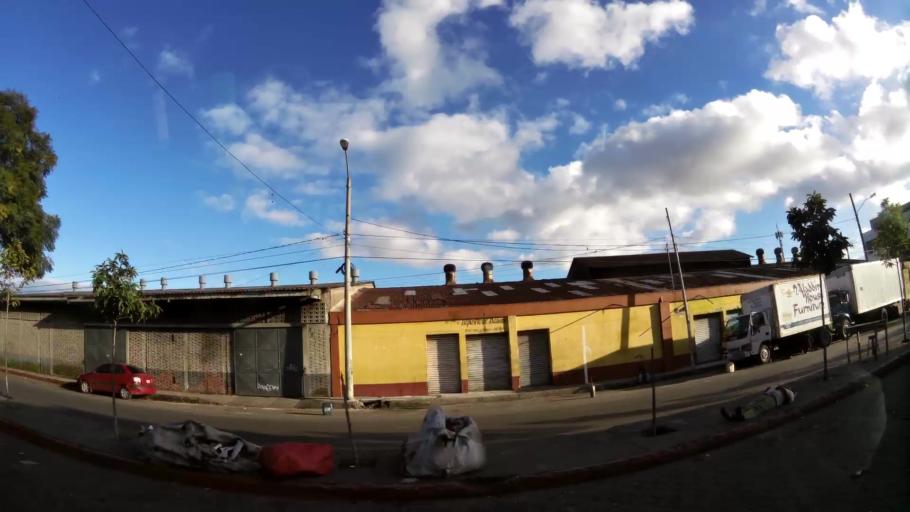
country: GT
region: Guatemala
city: Guatemala City
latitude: 14.6215
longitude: -90.5223
